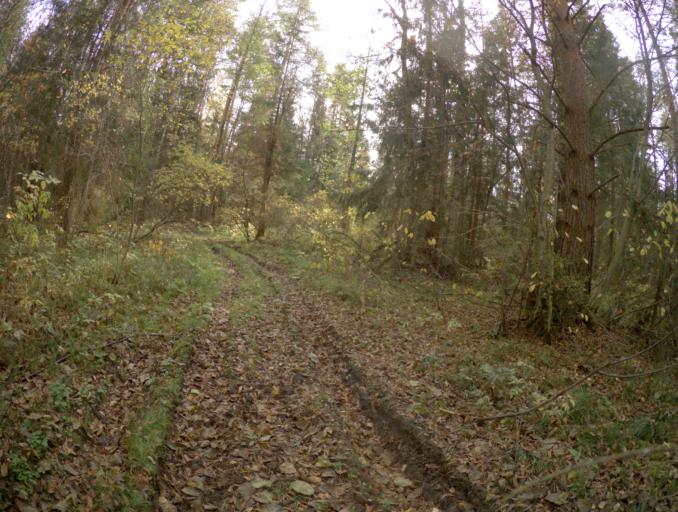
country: RU
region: Vladimir
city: Raduzhnyy
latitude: 55.9491
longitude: 40.3361
